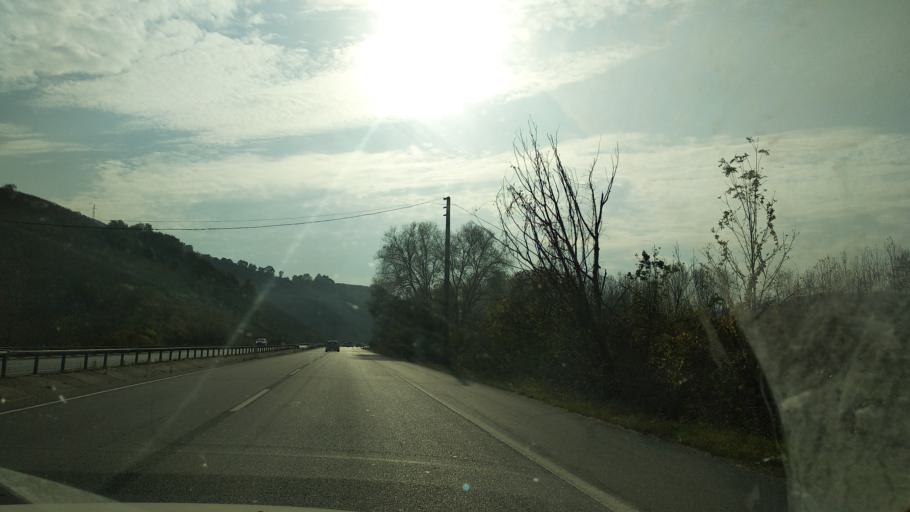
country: TR
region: Sakarya
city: Karasu
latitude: 41.0687
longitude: 30.6440
